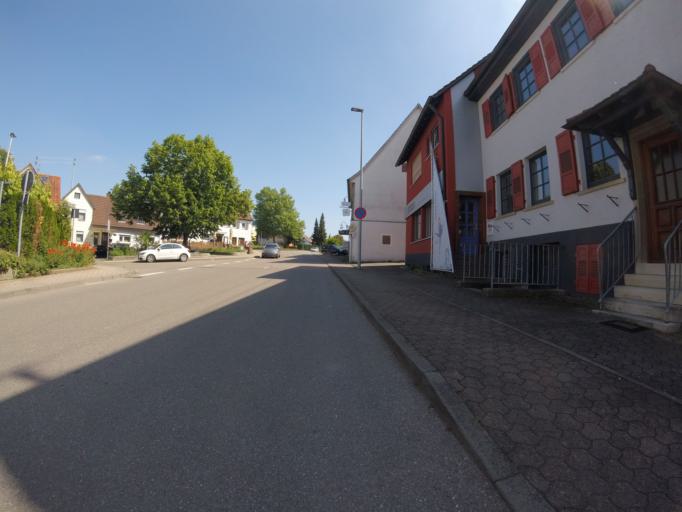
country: DE
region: Baden-Wuerttemberg
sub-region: Regierungsbezirk Stuttgart
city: Steinheim am der Murr
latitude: 48.9779
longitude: 9.2898
